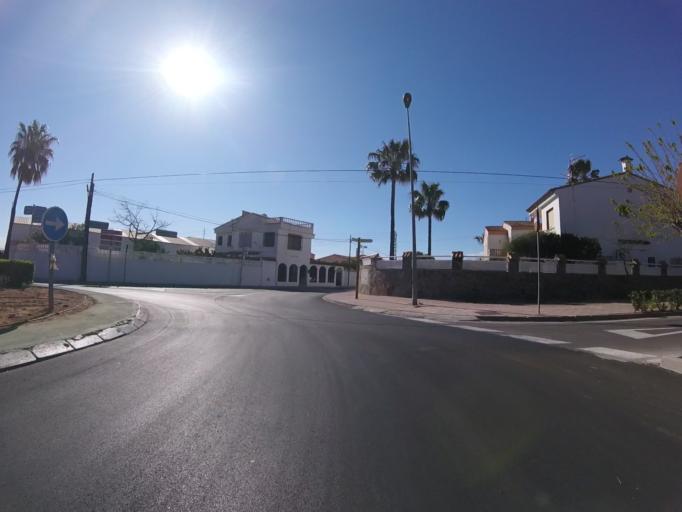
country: ES
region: Valencia
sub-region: Provincia de Castello
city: Orpesa/Oropesa del Mar
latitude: 40.0918
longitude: 0.1314
